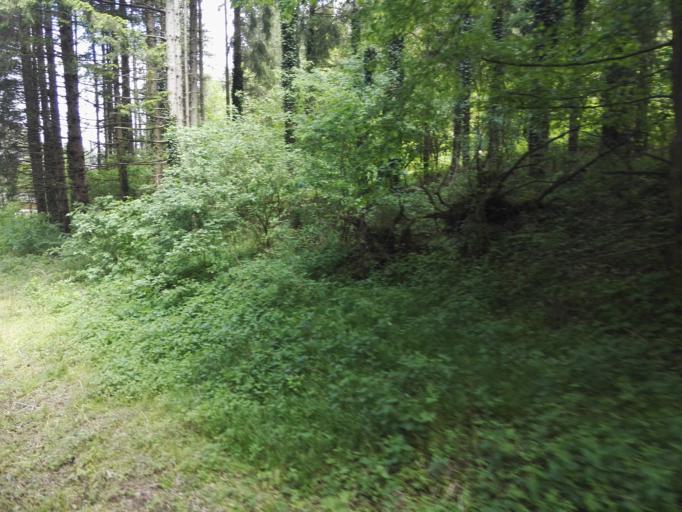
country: AT
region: Styria
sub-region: Politischer Bezirk Weiz
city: Koglhof
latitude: 47.3157
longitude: 15.6932
